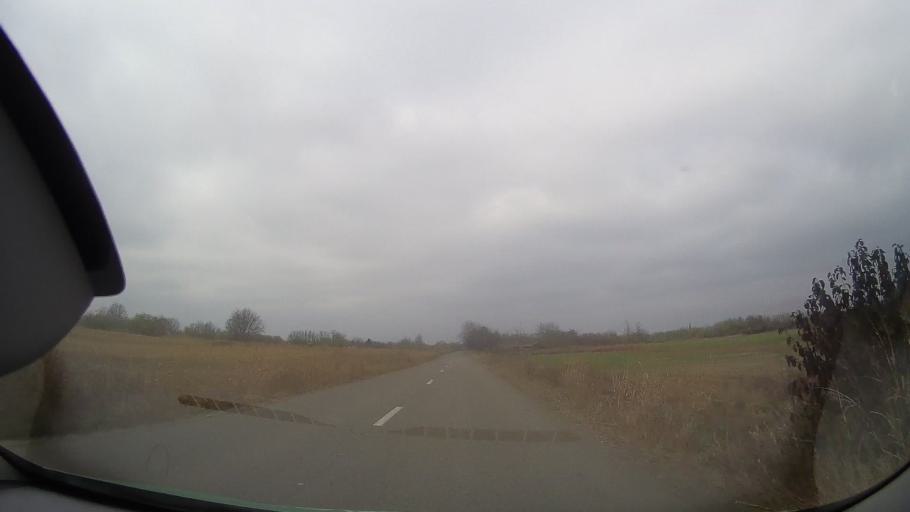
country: RO
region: Buzau
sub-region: Comuna Scutelnici
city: Scutelnici
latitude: 44.8741
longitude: 26.8842
